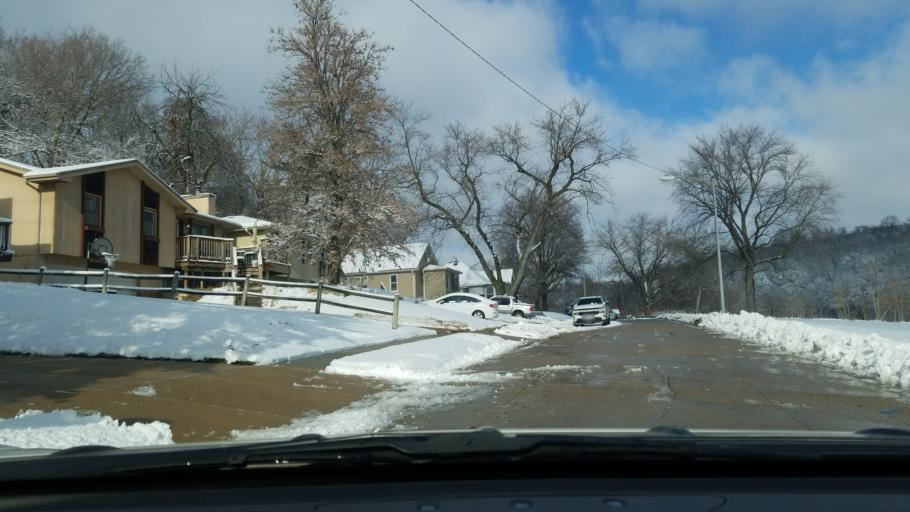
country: US
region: Nebraska
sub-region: Douglas County
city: Omaha
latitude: 41.2161
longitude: -95.9357
